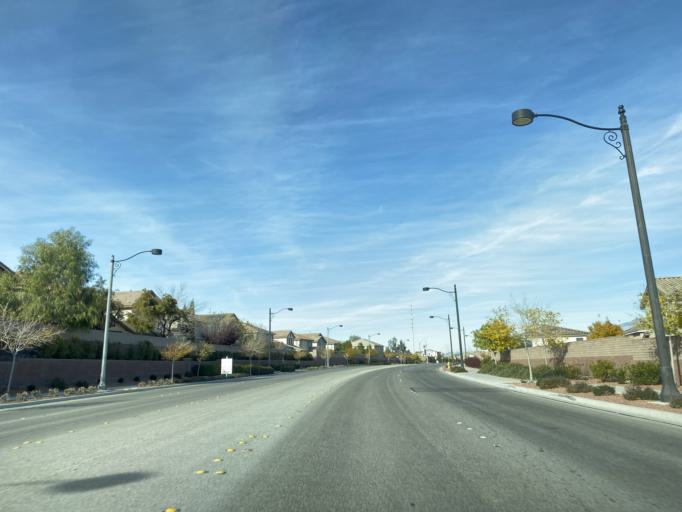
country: US
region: Nevada
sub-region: Clark County
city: Summerlin South
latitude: 36.3043
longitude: -115.3216
